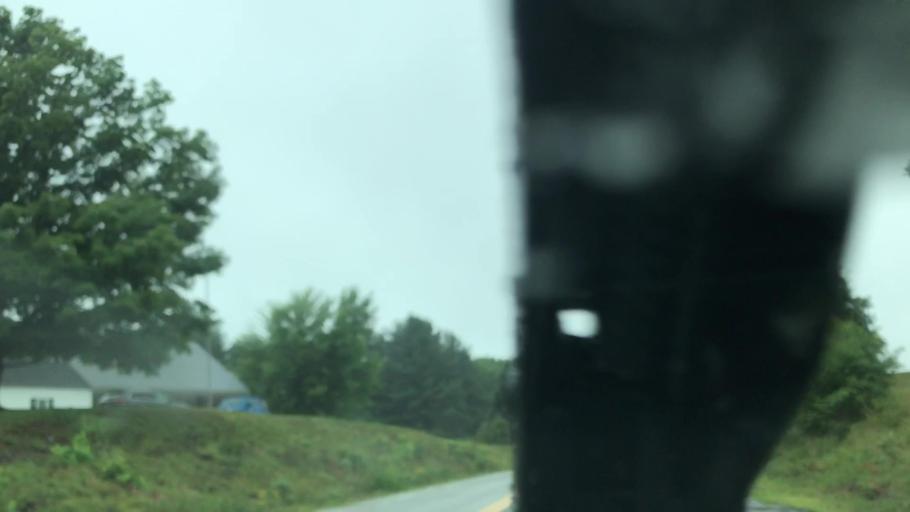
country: US
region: Maine
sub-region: York County
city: North Berwick
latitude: 43.2967
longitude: -70.7825
